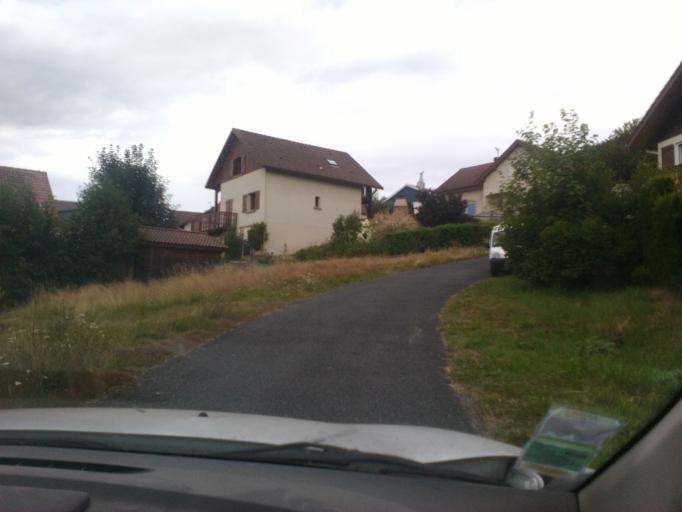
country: FR
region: Lorraine
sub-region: Departement des Vosges
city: Gerardmer
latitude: 48.0799
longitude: 6.8787
